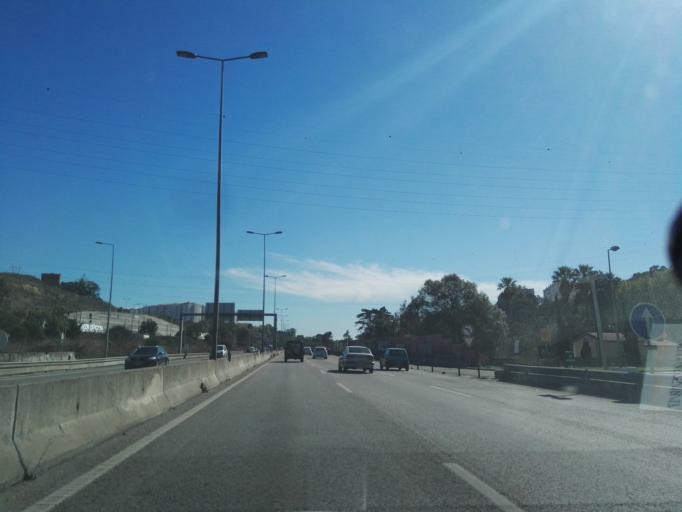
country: PT
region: Lisbon
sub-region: Sintra
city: Cacem
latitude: 38.7619
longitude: -9.2962
